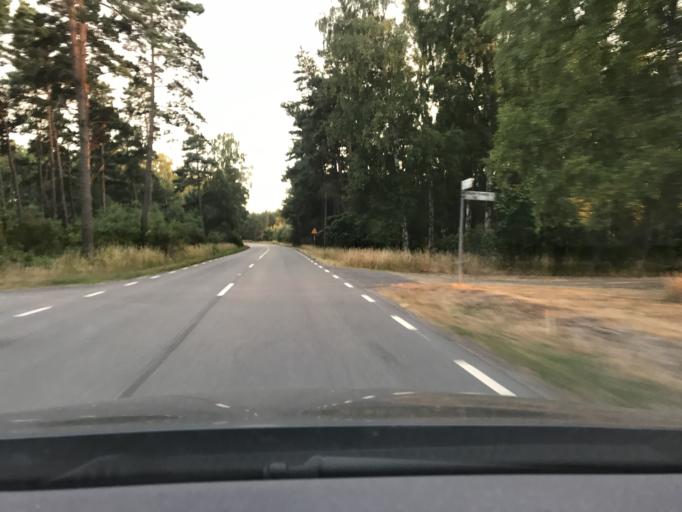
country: SE
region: Skane
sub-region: Simrishamns Kommun
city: Simrishamn
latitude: 55.4085
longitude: 14.1906
